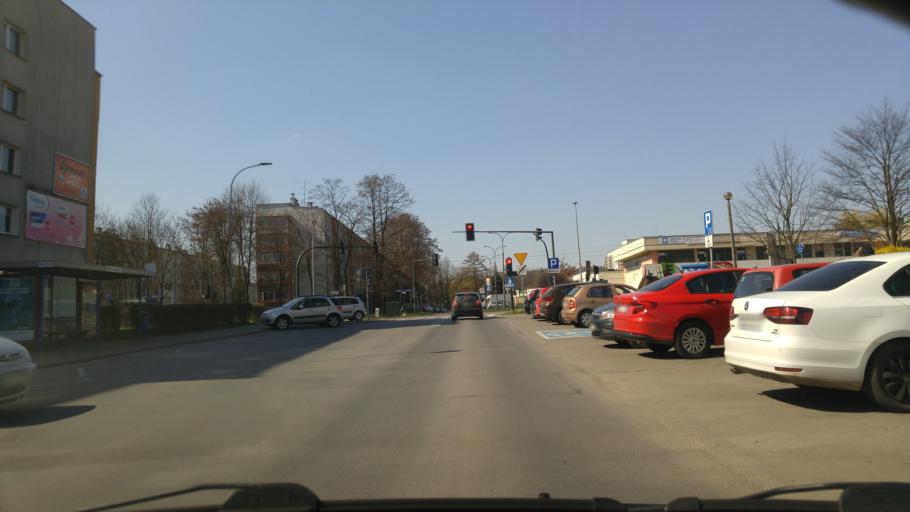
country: PL
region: Lesser Poland Voivodeship
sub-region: Powiat krakowski
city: Michalowice
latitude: 50.0982
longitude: 20.0141
